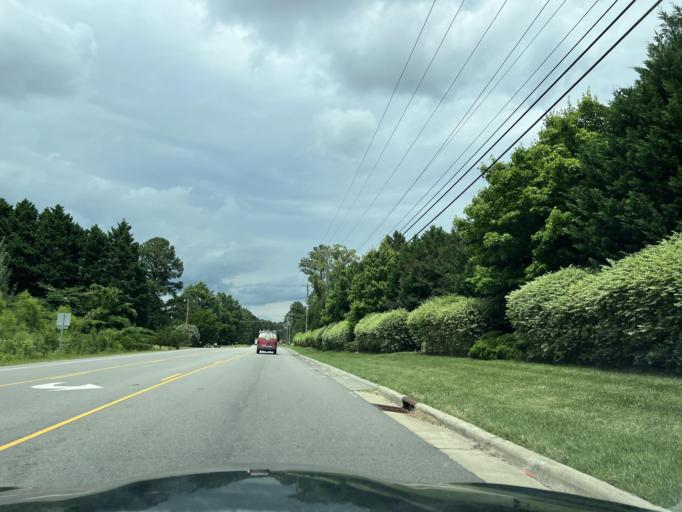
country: US
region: North Carolina
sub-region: Wake County
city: Morrisville
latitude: 35.9098
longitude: -78.8167
